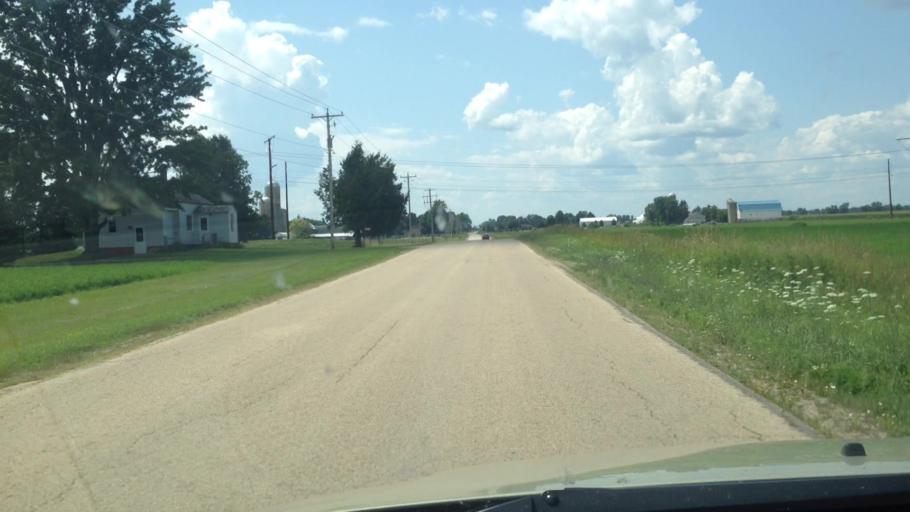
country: US
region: Wisconsin
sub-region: Brown County
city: Pulaski
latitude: 44.6564
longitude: -88.2504
